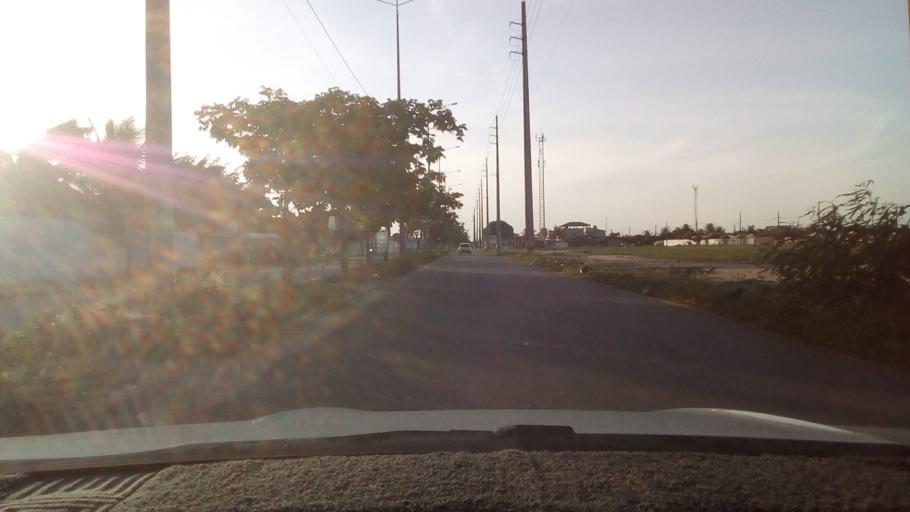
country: BR
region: Paraiba
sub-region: Conde
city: Conde
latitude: -7.1981
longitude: -34.8811
